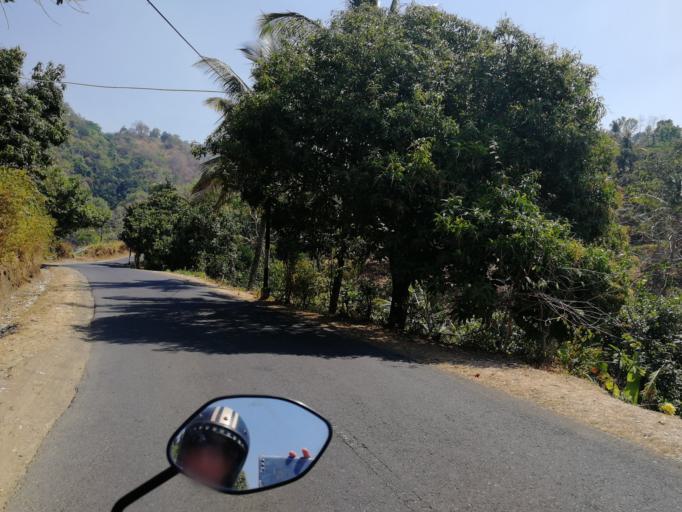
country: ID
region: Bali
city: Banjar Kedisan
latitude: -8.1404
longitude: 115.3195
